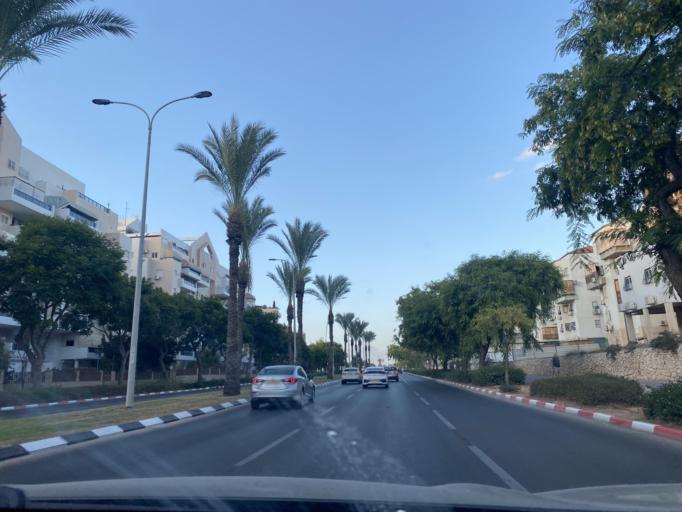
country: IL
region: Southern District
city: Ashdod
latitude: 31.7892
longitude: 34.6483
